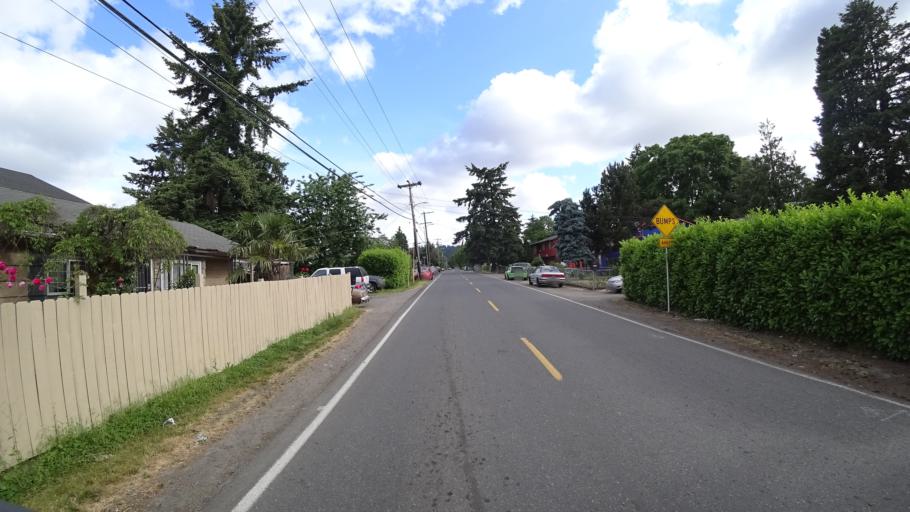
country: US
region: Oregon
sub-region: Multnomah County
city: Lents
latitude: 45.4827
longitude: -122.5557
